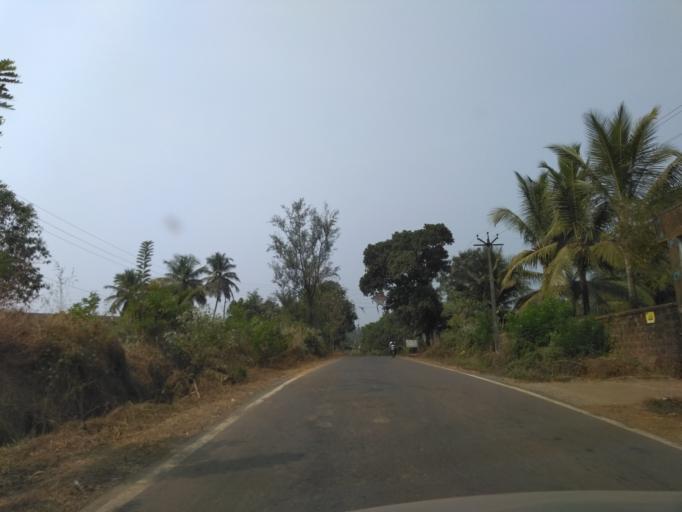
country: IN
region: Goa
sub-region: North Goa
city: Dicholi
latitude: 15.7308
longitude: 73.9496
